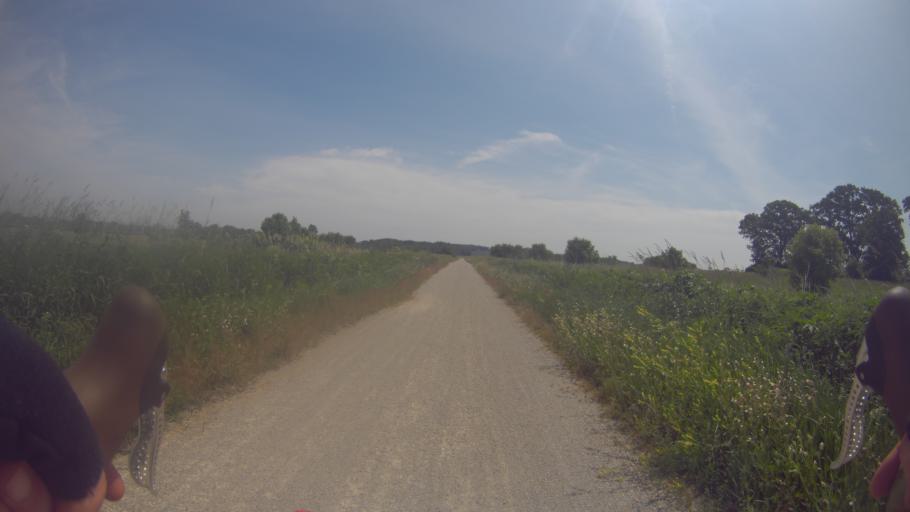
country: US
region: Wisconsin
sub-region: Jefferson County
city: Lake Ripley
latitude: 43.0583
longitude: -88.9728
